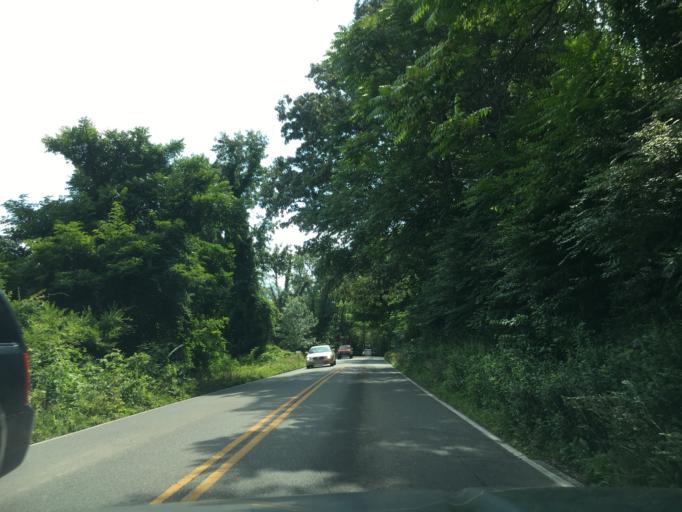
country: US
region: Virginia
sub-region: Roanoke County
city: Cave Spring
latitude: 37.2039
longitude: -80.0042
